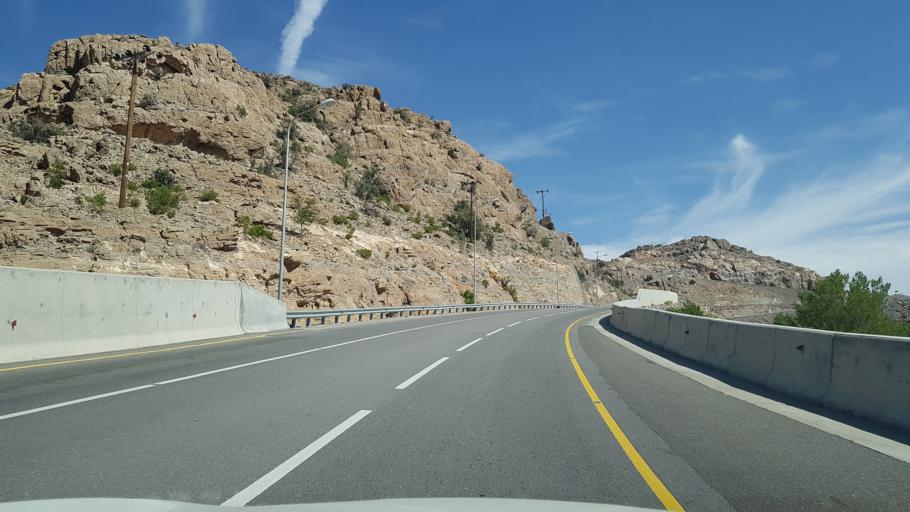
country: OM
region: Muhafazat ad Dakhiliyah
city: Izki
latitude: 23.0647
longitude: 57.7254
